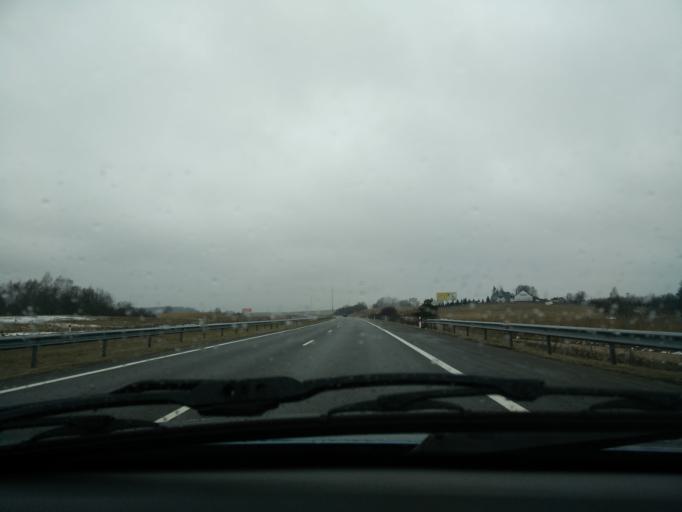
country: LT
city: Silale
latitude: 55.5542
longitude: 22.2552
